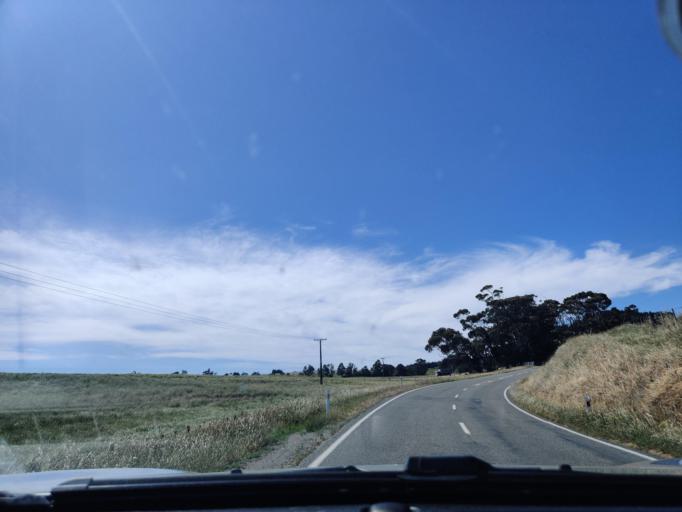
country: NZ
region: Wellington
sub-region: South Wairarapa District
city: Waipawa
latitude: -41.2018
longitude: 175.3640
